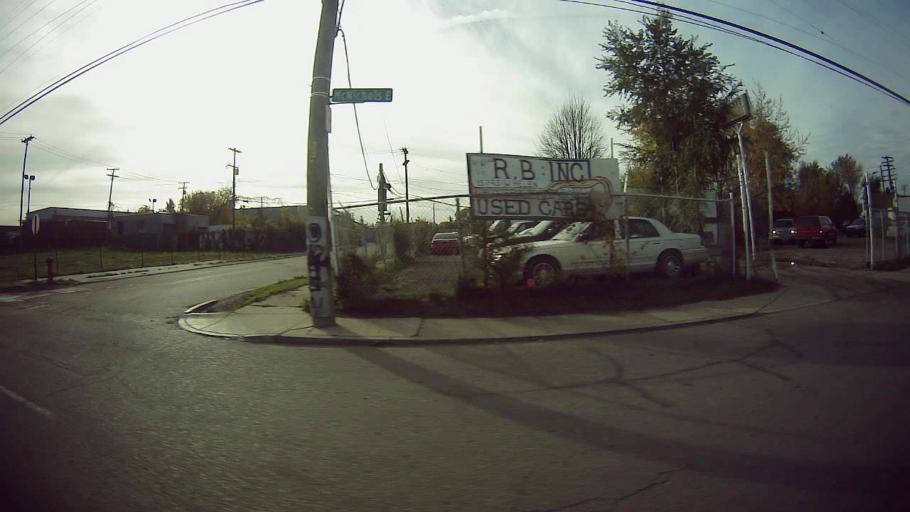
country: US
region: Michigan
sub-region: Wayne County
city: Hamtramck
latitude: 42.4194
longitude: -83.0311
